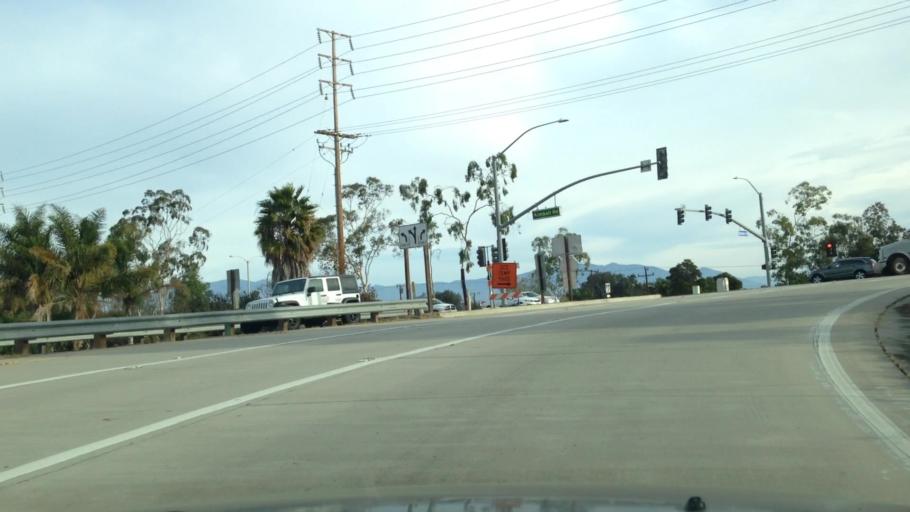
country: US
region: California
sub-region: Ventura County
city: Saticoy
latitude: 34.2756
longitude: -119.1921
